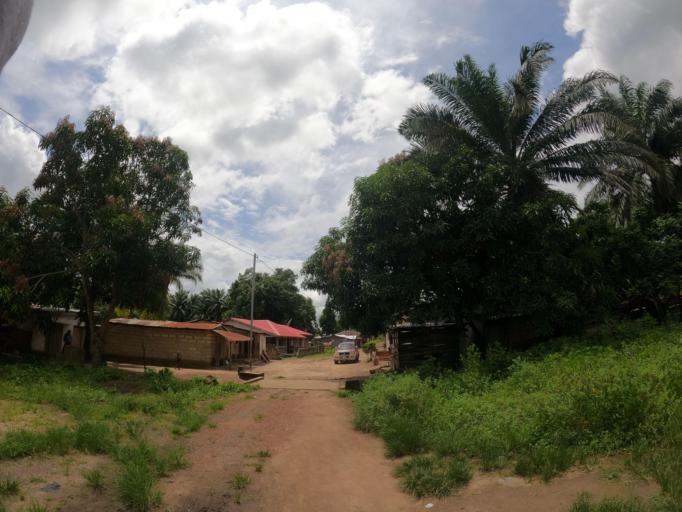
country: SL
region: Northern Province
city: Binkolo
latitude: 9.1071
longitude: -12.2055
